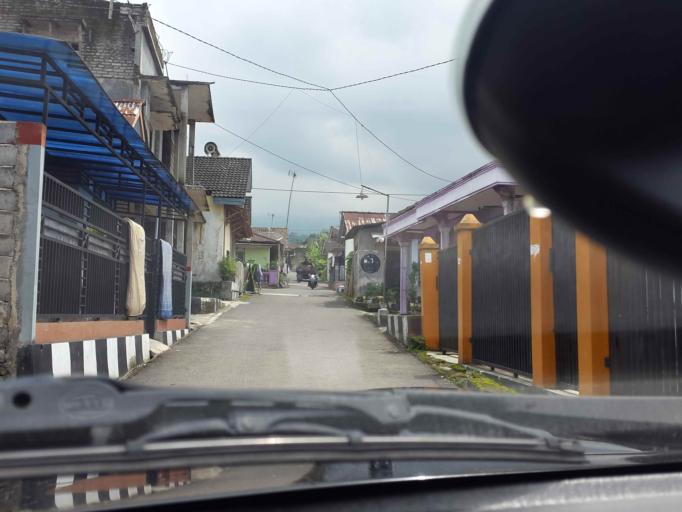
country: ID
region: Central Java
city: Wonosobo
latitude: -7.3713
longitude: 109.9530
